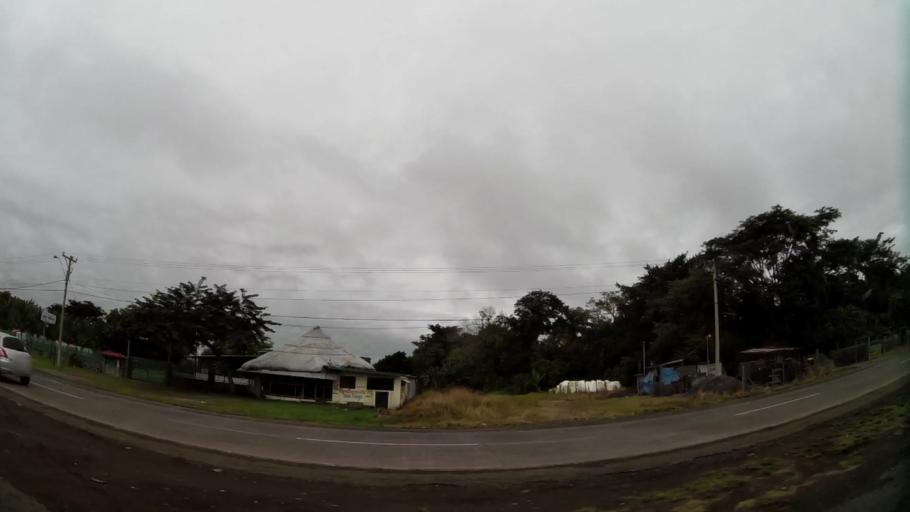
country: PA
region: Chiriqui
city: La Concepcion
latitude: 8.5060
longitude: -82.6090
